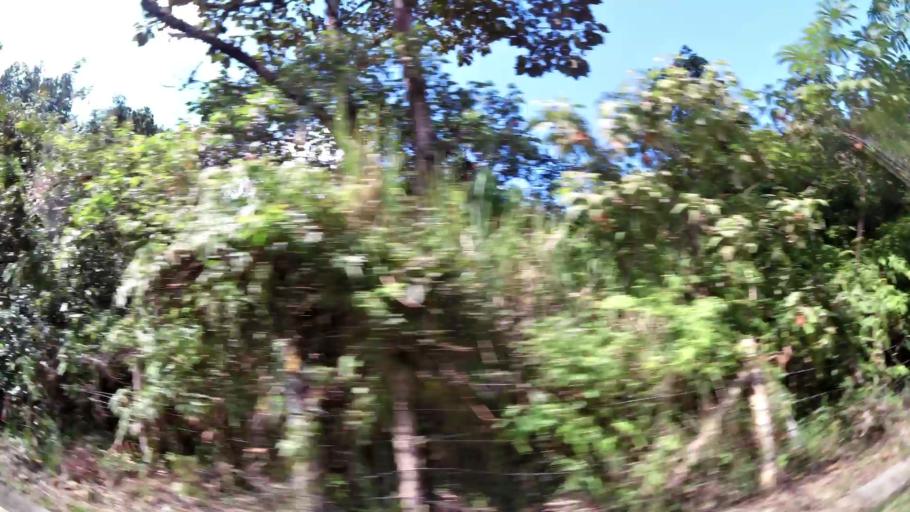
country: CO
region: Valle del Cauca
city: Cali
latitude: 3.4291
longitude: -76.5679
